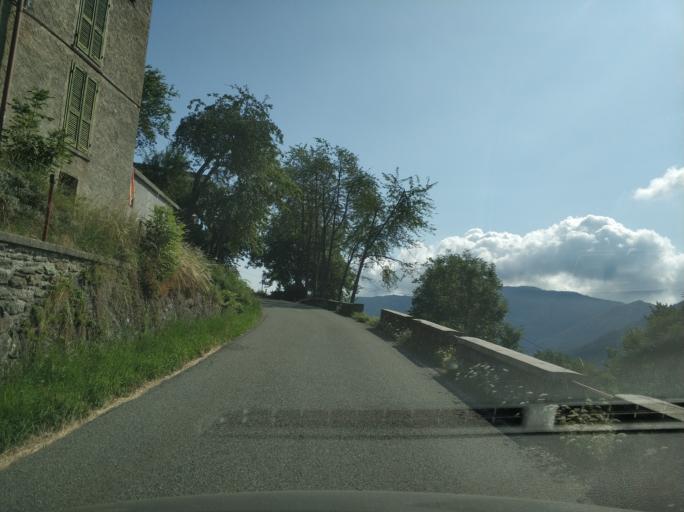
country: IT
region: Piedmont
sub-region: Provincia di Torino
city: Viu
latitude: 45.1922
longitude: 7.3690
